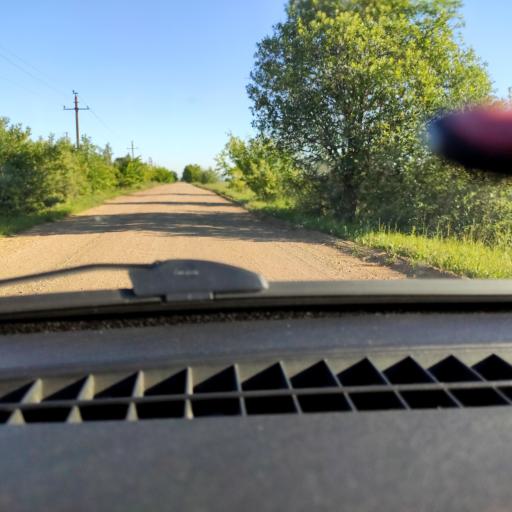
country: RU
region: Bashkortostan
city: Iglino
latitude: 54.7530
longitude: 56.3368
